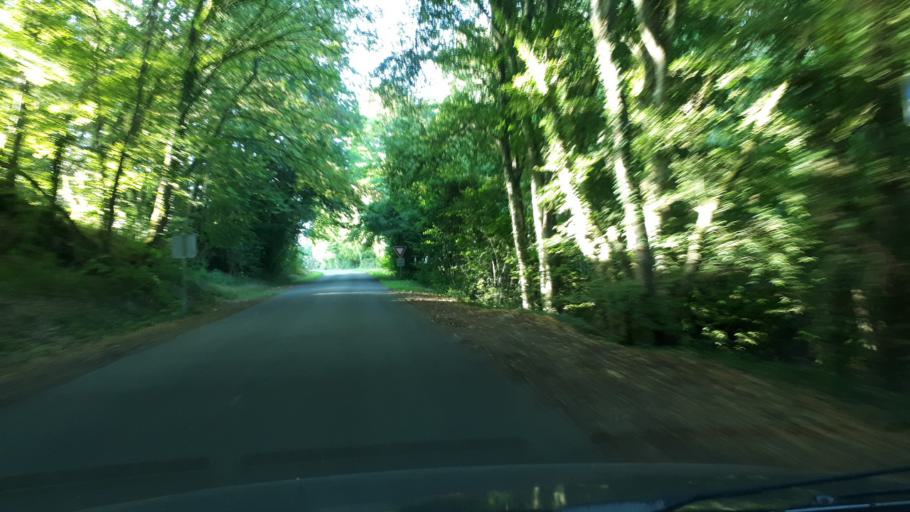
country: FR
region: Centre
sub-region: Departement du Loir-et-Cher
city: Villiers-sur-Loir
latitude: 47.7668
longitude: 0.9589
